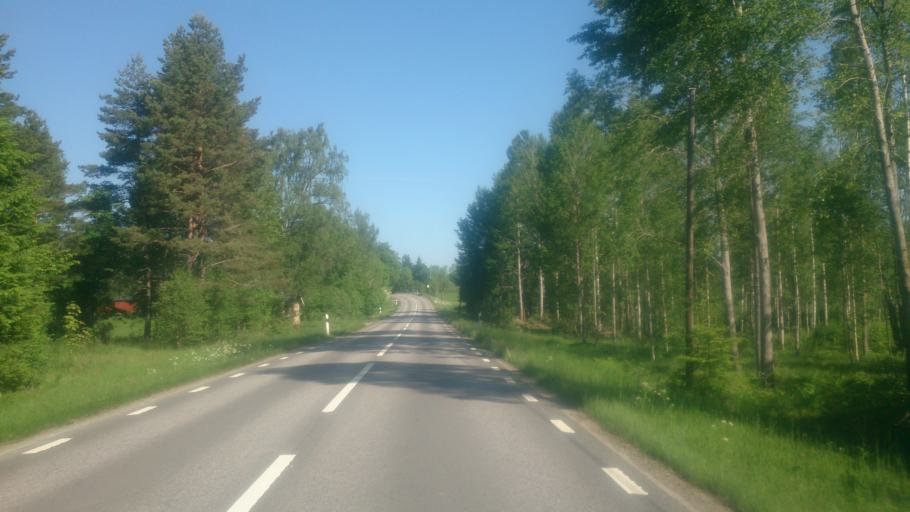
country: SE
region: OEstergoetland
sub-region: Atvidabergs Kommun
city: Atvidaberg
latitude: 58.1348
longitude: 16.0915
